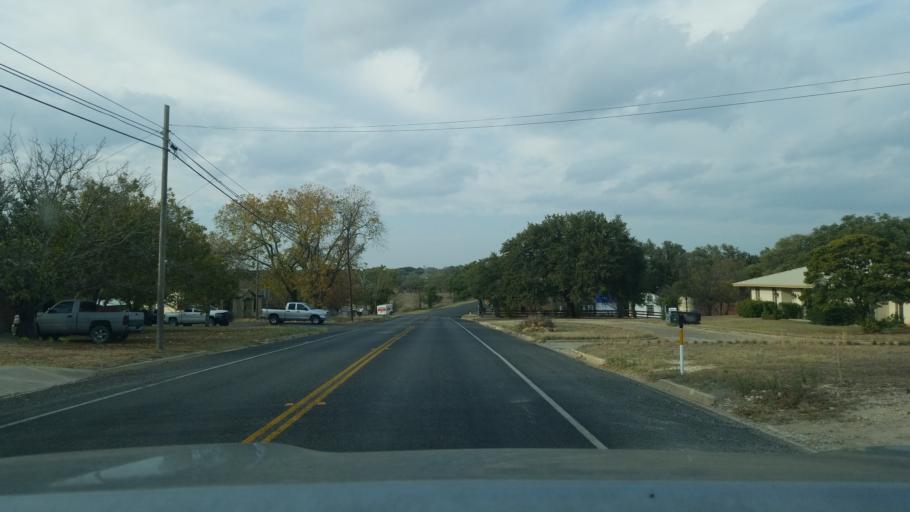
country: US
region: Texas
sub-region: Mills County
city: Goldthwaite
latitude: 31.4608
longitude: -98.5736
